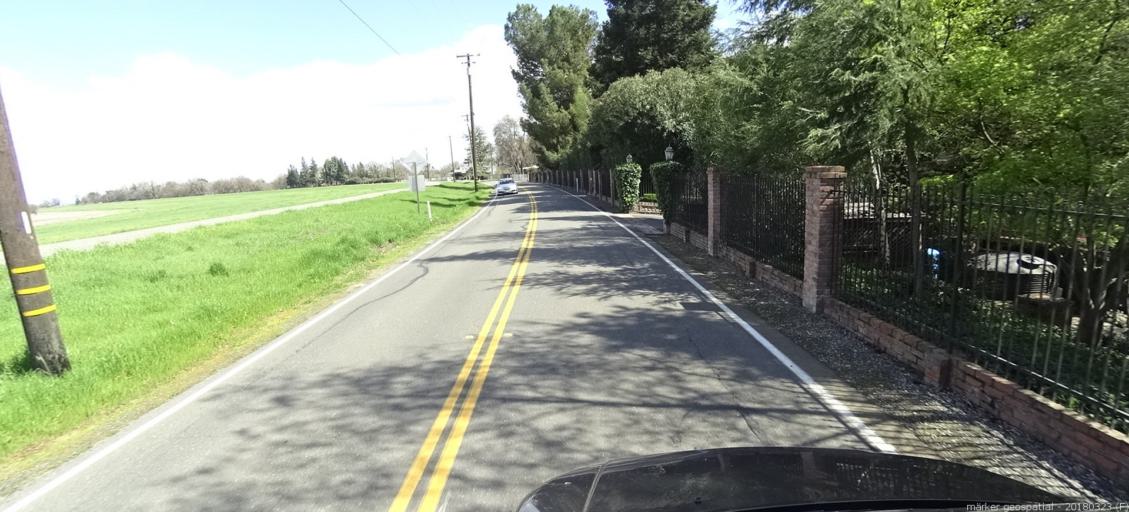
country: US
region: California
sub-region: Yolo County
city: West Sacramento
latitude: 38.6444
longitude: -121.5917
